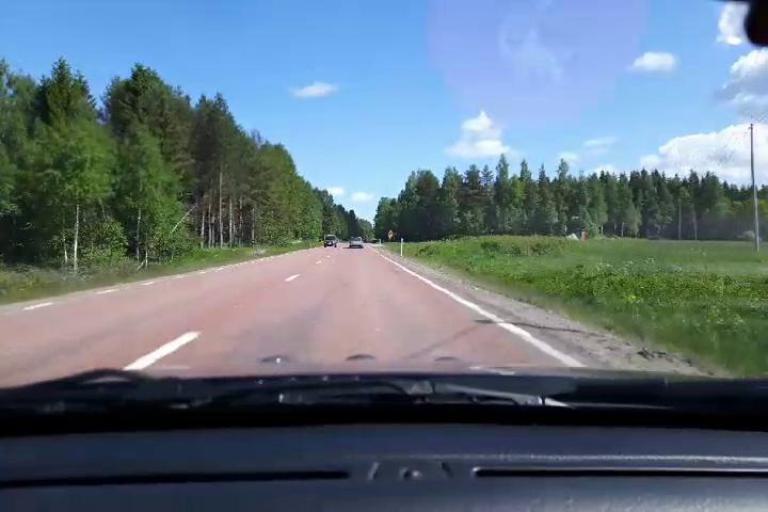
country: SE
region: Gaevleborg
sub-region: Hudiksvalls Kommun
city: Delsbo
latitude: 61.7679
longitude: 16.7024
